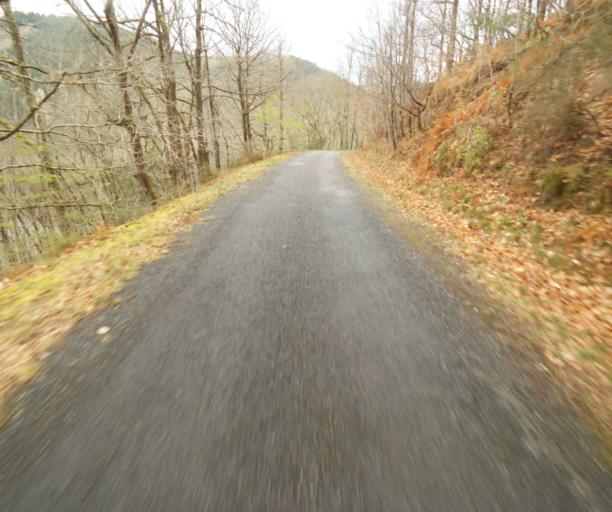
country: FR
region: Limousin
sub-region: Departement de la Correze
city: Saint-Privat
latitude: 45.2116
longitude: 2.0353
